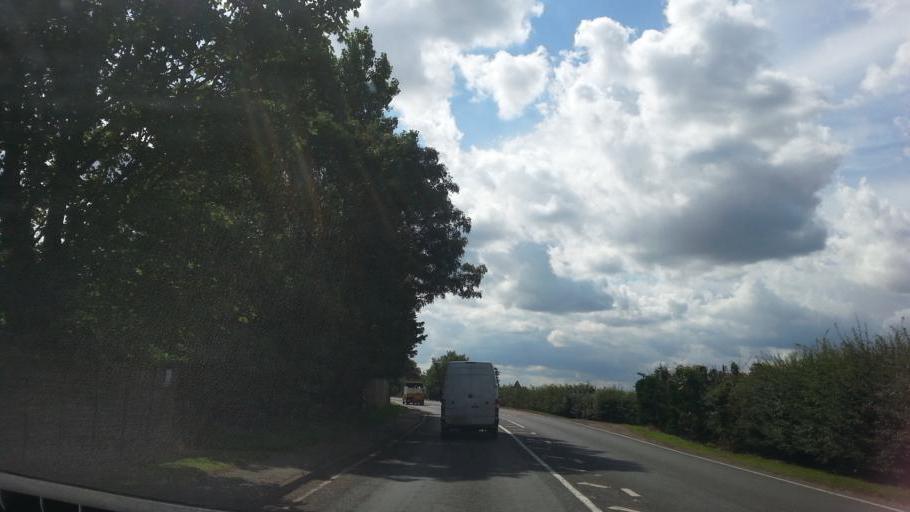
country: GB
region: England
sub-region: Nottinghamshire
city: Newark on Trent
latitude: 53.1061
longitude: -0.8225
